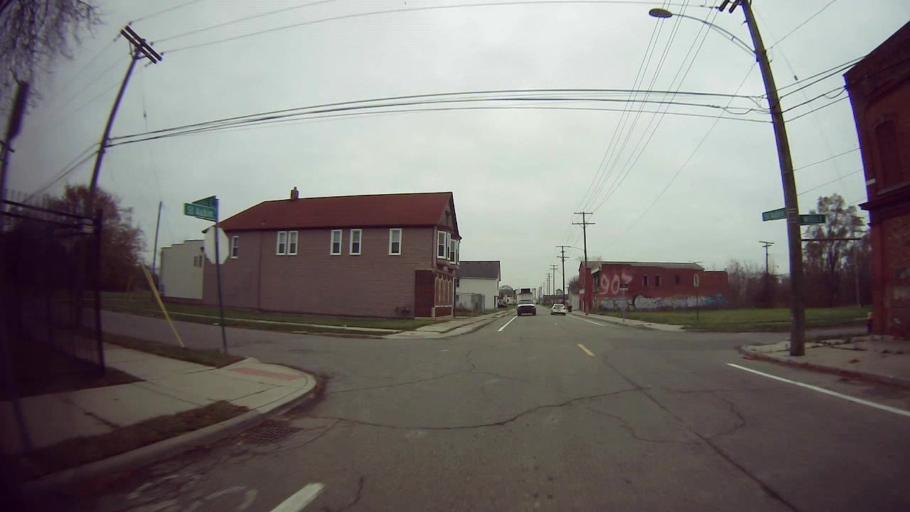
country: US
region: Michigan
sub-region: Wayne County
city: Detroit
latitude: 42.3594
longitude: -83.0410
